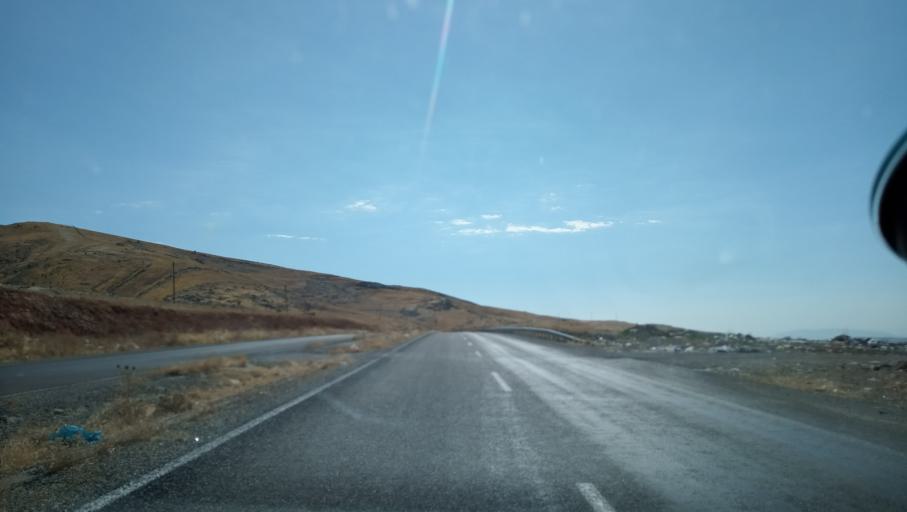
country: TR
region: Diyarbakir
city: Silvan
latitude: 38.1278
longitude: 41.0837
